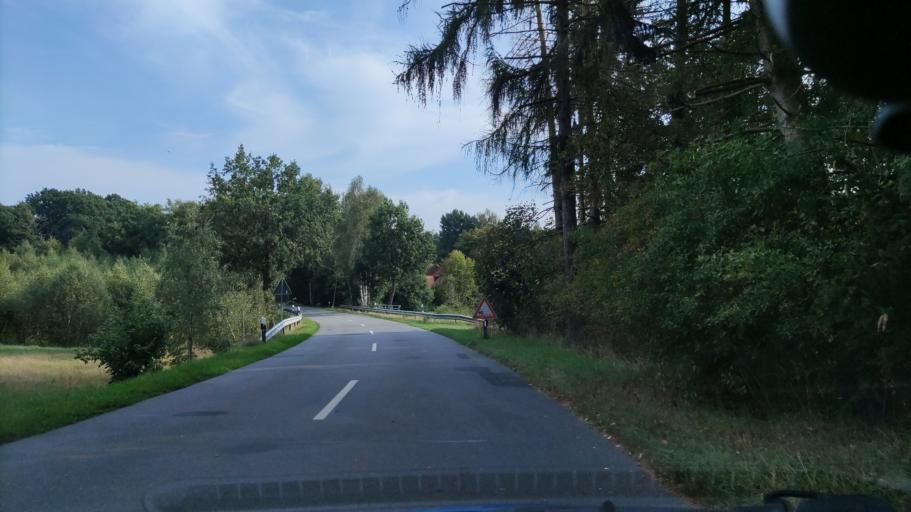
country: DE
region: Lower Saxony
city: Gerdau
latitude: 52.9736
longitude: 10.3730
